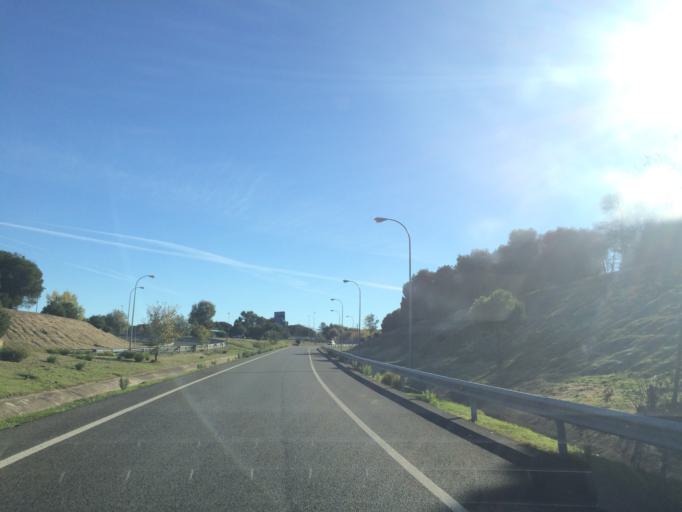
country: ES
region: Madrid
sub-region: Provincia de Madrid
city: Alcorcon
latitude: 40.3722
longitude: -3.8030
